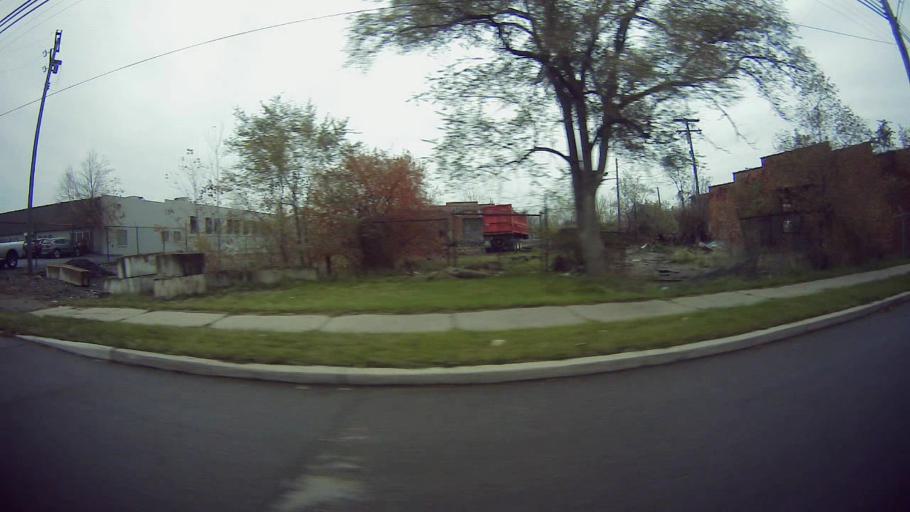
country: US
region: Michigan
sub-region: Wayne County
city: Highland Park
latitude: 42.4159
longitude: -83.0817
